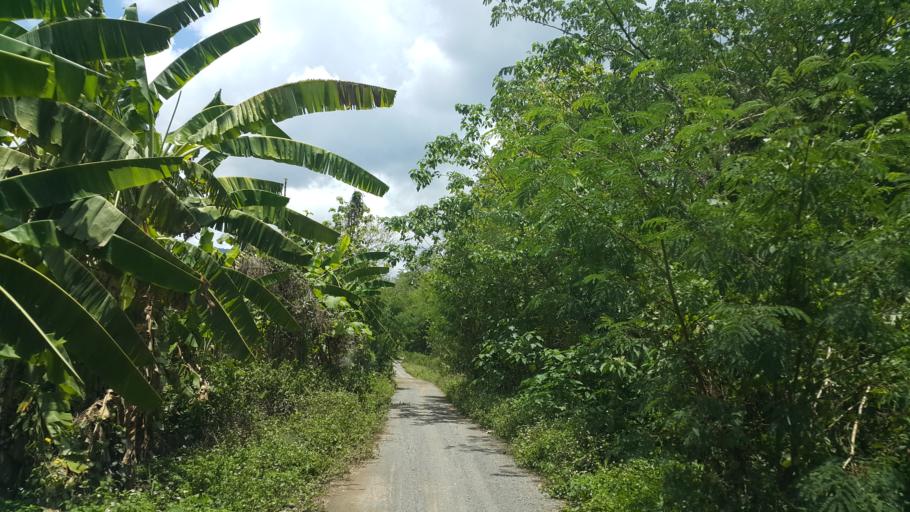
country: TH
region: Phayao
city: Phayao
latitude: 19.1784
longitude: 99.7767
